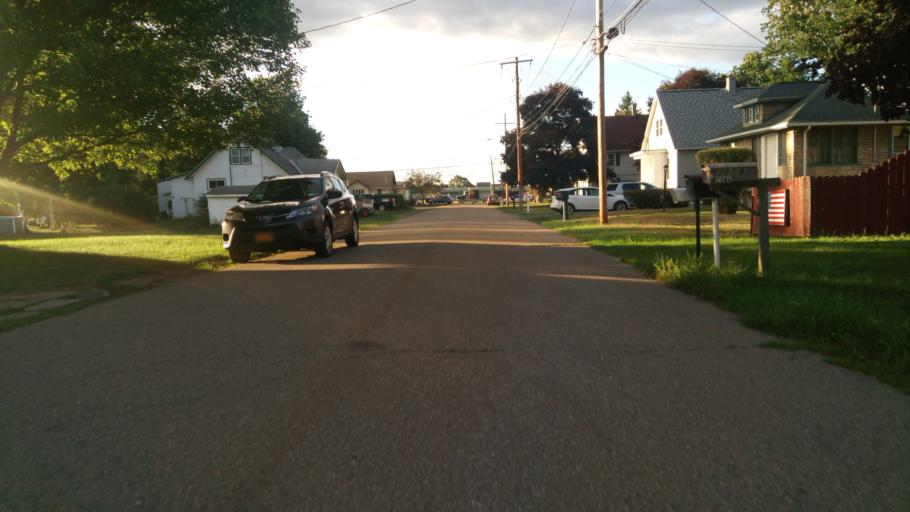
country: US
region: New York
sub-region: Chemung County
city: Southport
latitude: 42.0625
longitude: -76.7935
